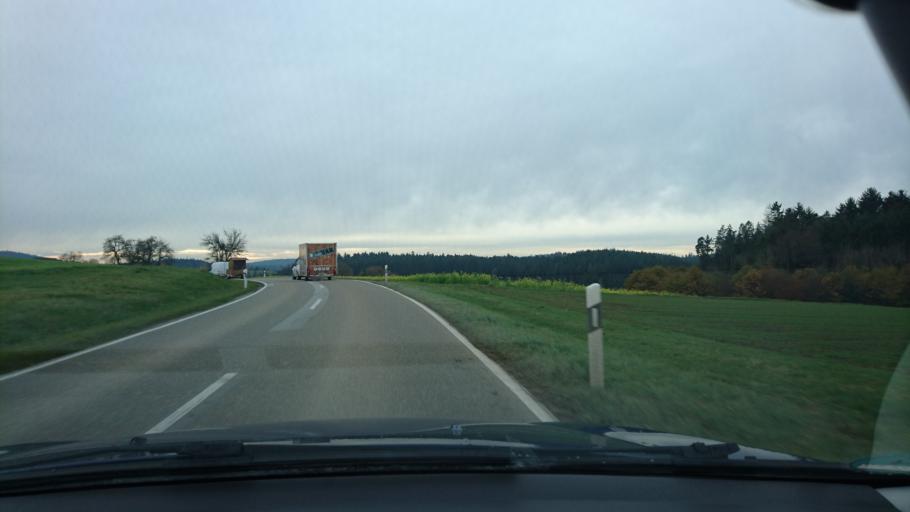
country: DE
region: Baden-Wuerttemberg
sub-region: Regierungsbezirk Stuttgart
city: Gschwend
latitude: 48.9176
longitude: 9.7050
